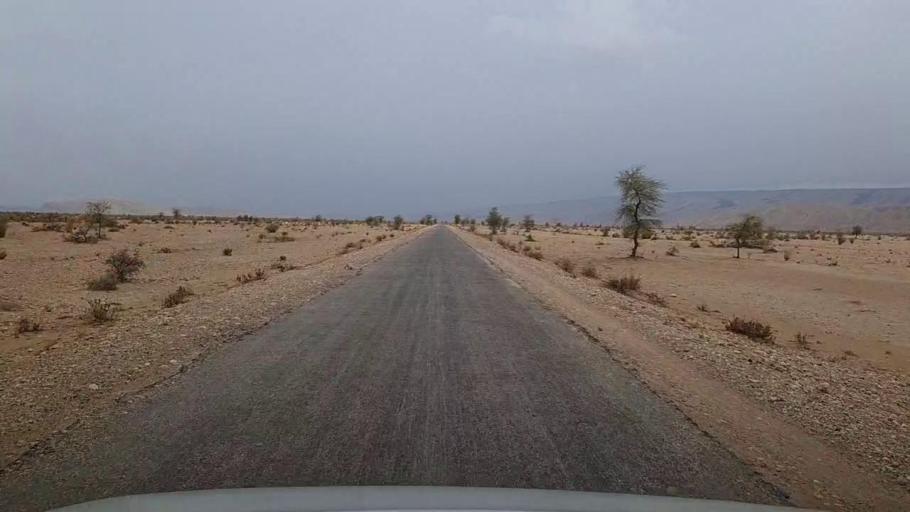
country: PK
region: Sindh
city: Sehwan
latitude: 26.2666
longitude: 67.7235
